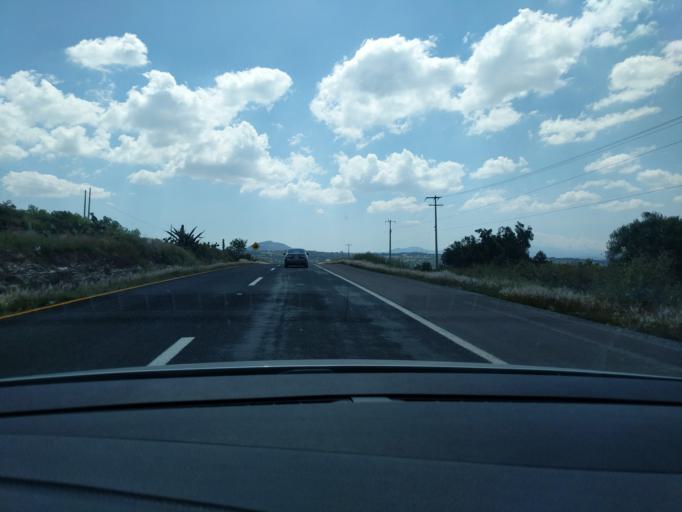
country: MX
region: Hidalgo
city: Zempoala
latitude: 19.8900
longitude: -98.6686
